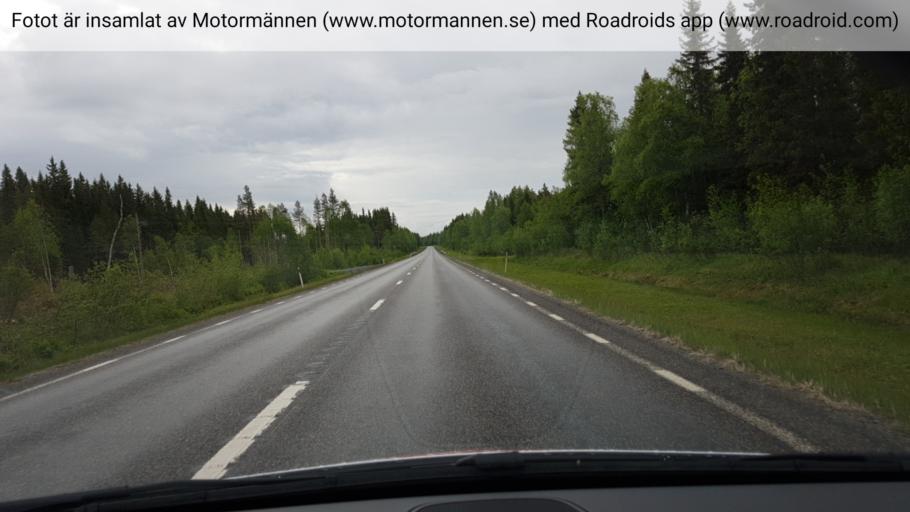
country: SE
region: Jaemtland
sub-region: OEstersunds Kommun
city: Brunflo
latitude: 63.2014
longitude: 14.9352
